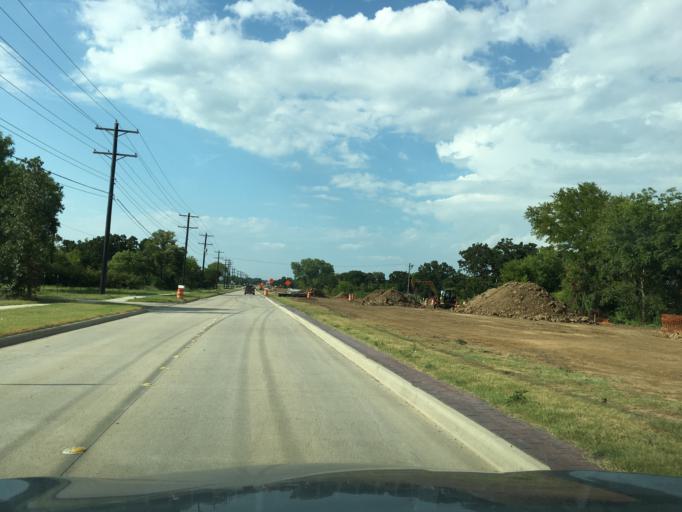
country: US
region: Texas
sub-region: Denton County
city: Denton
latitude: 33.2211
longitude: -97.0835
